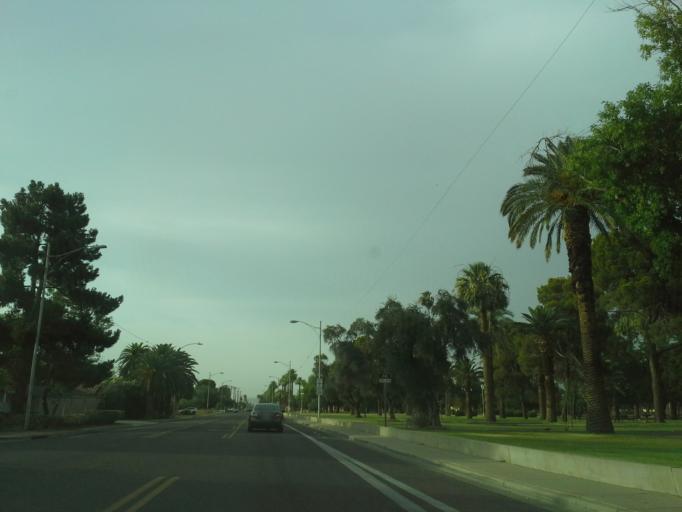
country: US
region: Arizona
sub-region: Maricopa County
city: Phoenix
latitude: 33.4739
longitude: -112.0913
